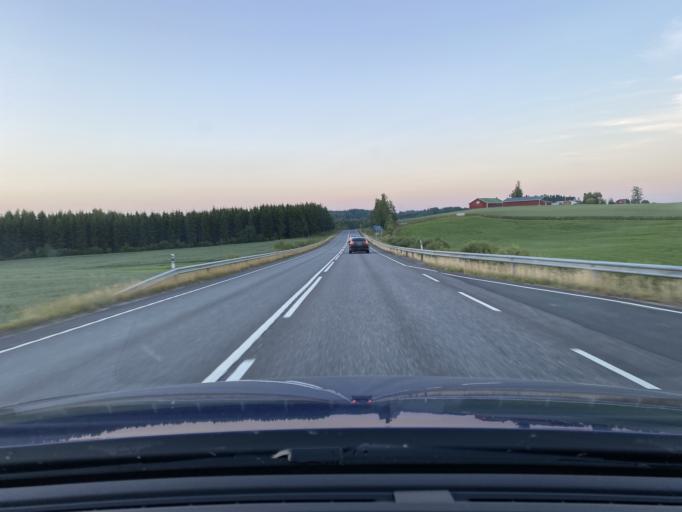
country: FI
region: Pirkanmaa
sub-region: Luoteis-Pirkanmaa
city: Ikaalinen
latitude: 61.8605
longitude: 22.9525
